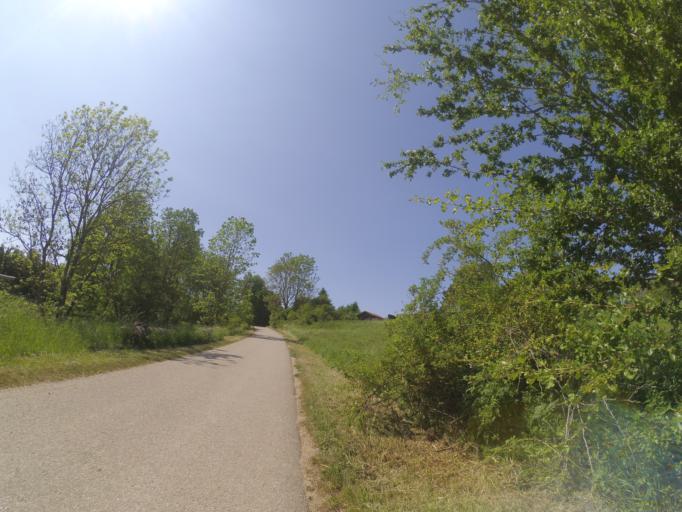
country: DE
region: Baden-Wuerttemberg
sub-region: Tuebingen Region
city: Merklingen
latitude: 48.5084
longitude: 9.7629
